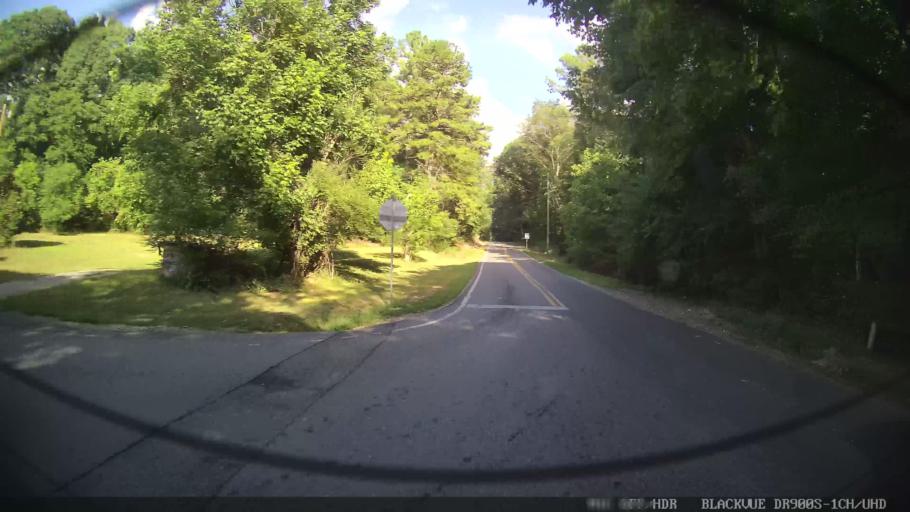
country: US
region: Georgia
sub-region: Floyd County
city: Lindale
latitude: 34.2108
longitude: -85.1250
